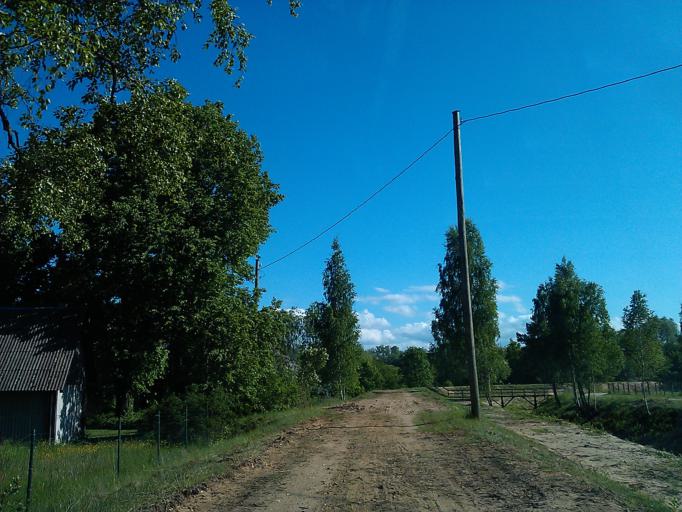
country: LV
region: Adazi
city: Adazi
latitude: 57.0971
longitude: 24.3299
